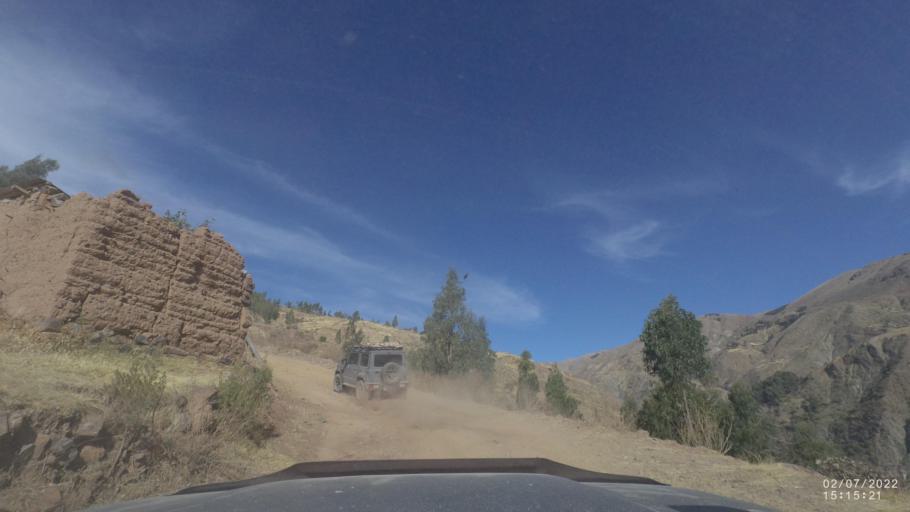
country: BO
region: Cochabamba
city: Irpa Irpa
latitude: -17.8641
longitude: -66.4352
